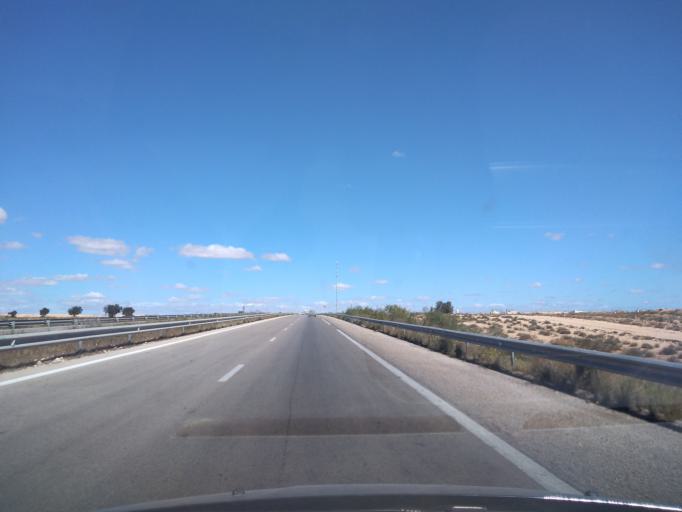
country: TN
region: Safaqis
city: Al Qarmadah
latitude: 34.9304
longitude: 10.7381
